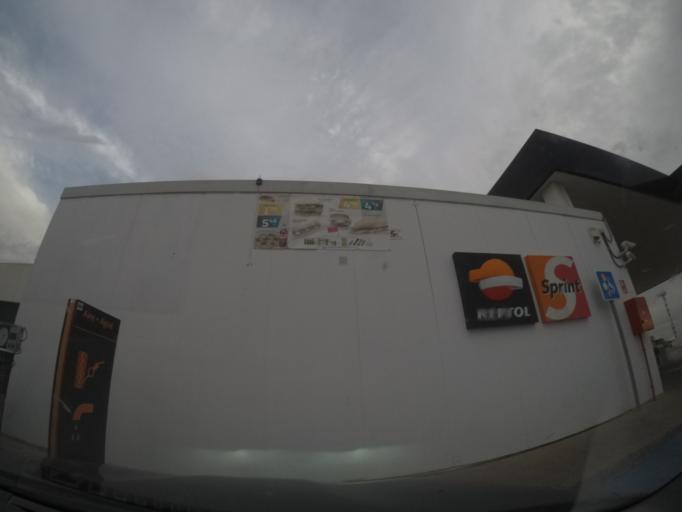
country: ES
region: Andalusia
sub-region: Provincia de Huelva
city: Chucena
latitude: 37.3482
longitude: -6.4233
